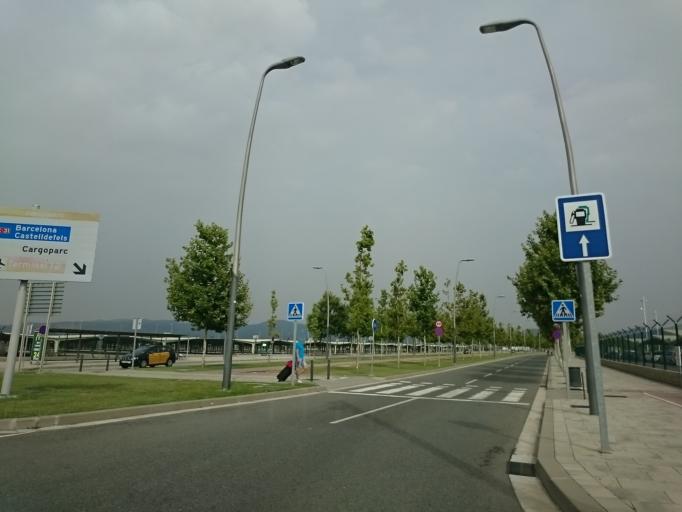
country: ES
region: Catalonia
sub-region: Provincia de Barcelona
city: Viladecans
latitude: 41.2916
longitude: 2.0550
